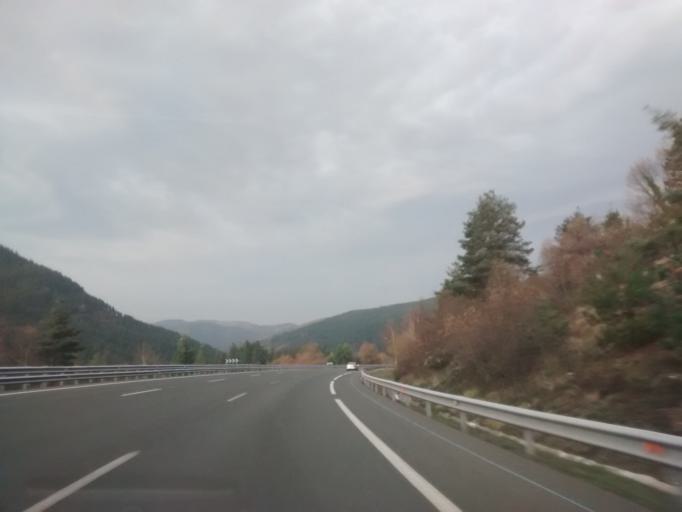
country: ES
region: Basque Country
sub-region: Provincia de Alava
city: Lezama
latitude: 43.0218
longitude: -2.9121
